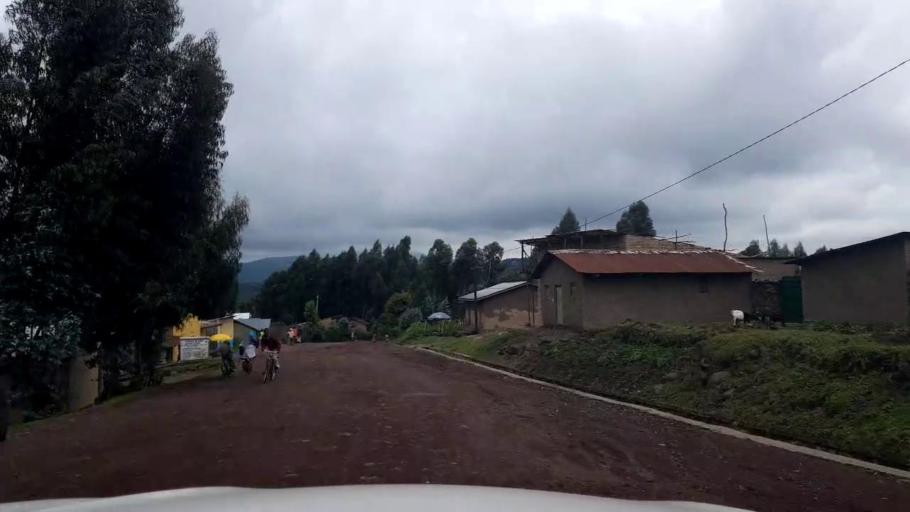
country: RW
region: Northern Province
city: Musanze
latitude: -1.6011
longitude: 29.4521
